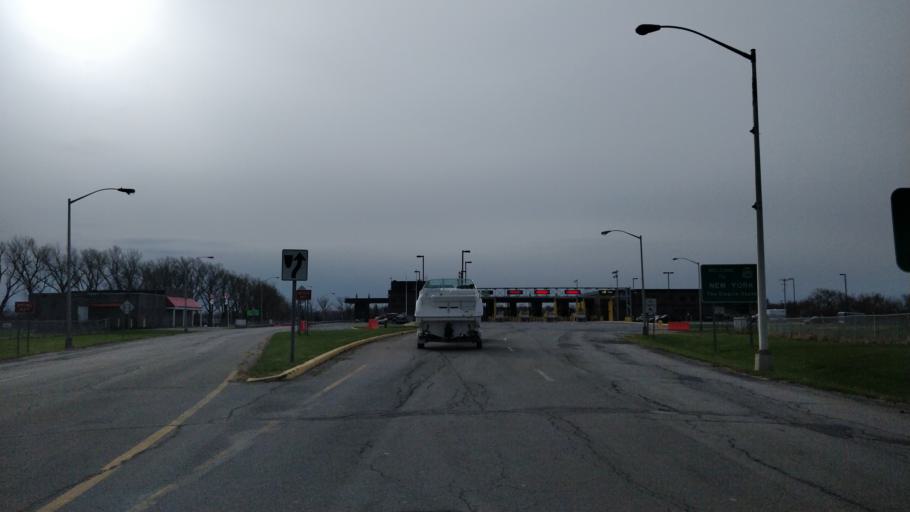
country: US
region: New York
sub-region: St. Lawrence County
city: Ogdensburg
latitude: 44.7236
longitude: -75.4548
